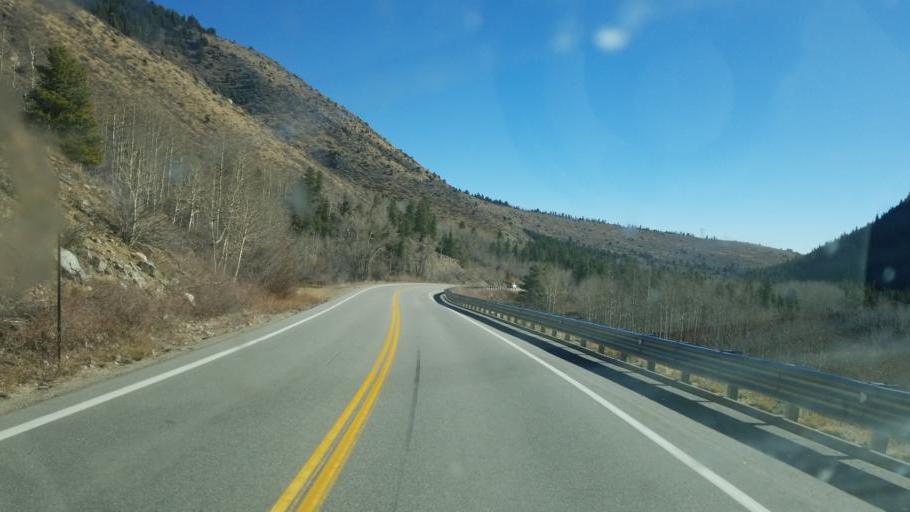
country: US
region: Colorado
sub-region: Chaffee County
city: Salida
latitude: 38.5497
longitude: -106.2684
